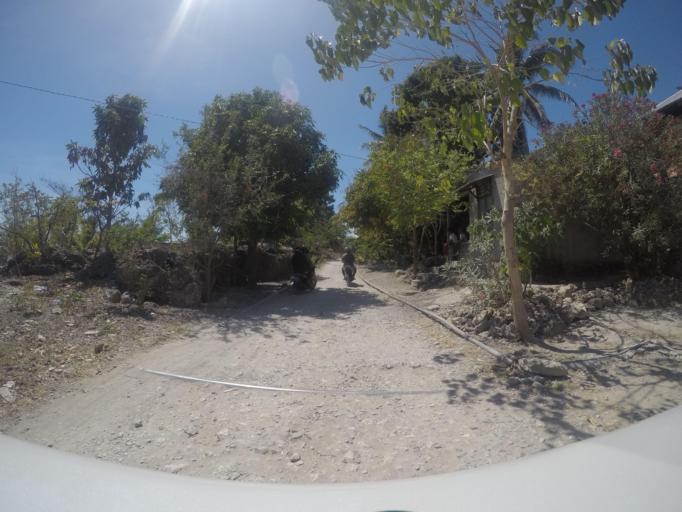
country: TL
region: Baucau
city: Baucau
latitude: -8.4669
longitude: 126.4573
